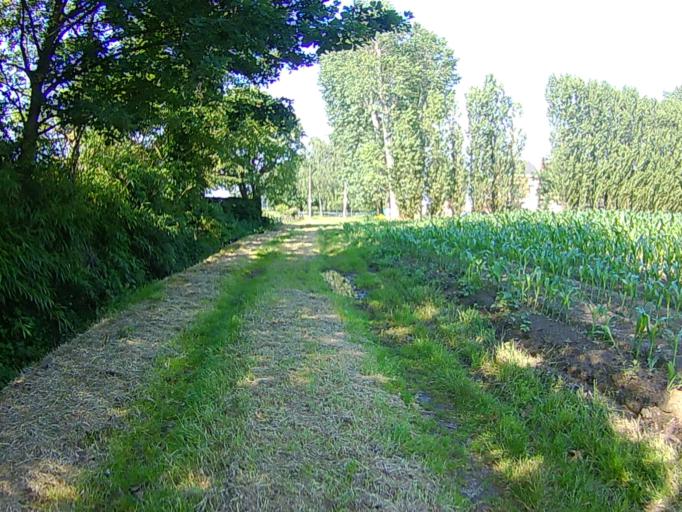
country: BE
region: Flanders
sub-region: Provincie Antwerpen
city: Zwijndrecht
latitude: 51.2041
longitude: 4.3329
